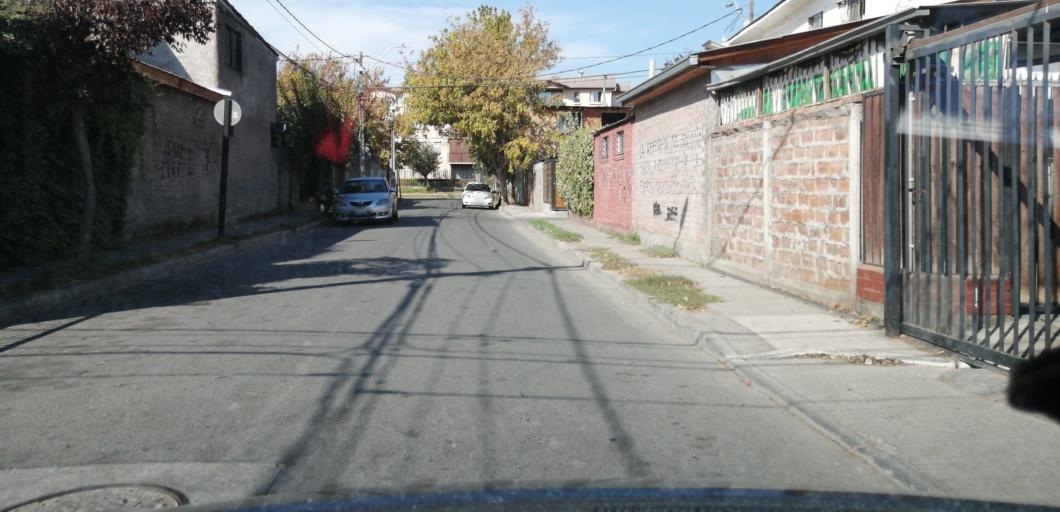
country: CL
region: Santiago Metropolitan
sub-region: Provincia de Santiago
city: Lo Prado
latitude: -33.4591
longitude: -70.7356
